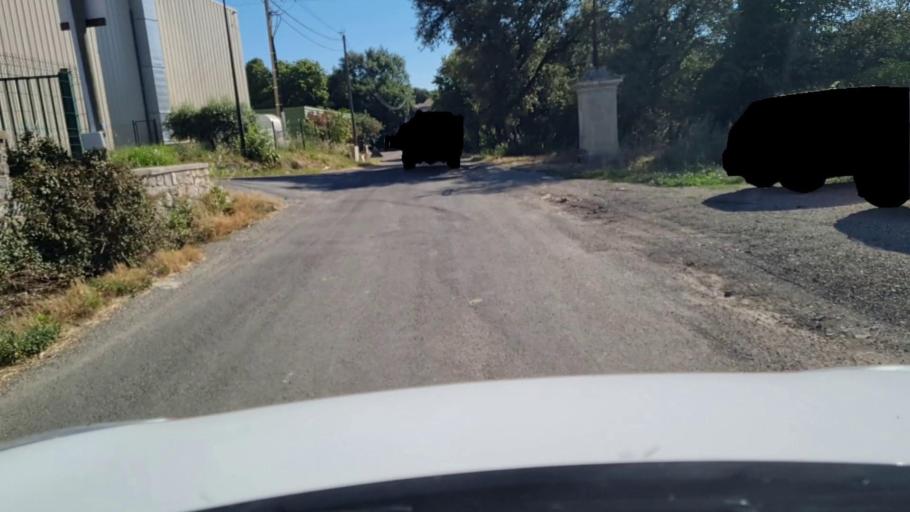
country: FR
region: Languedoc-Roussillon
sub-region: Departement du Gard
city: Sommieres
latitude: 43.8071
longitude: 4.0442
